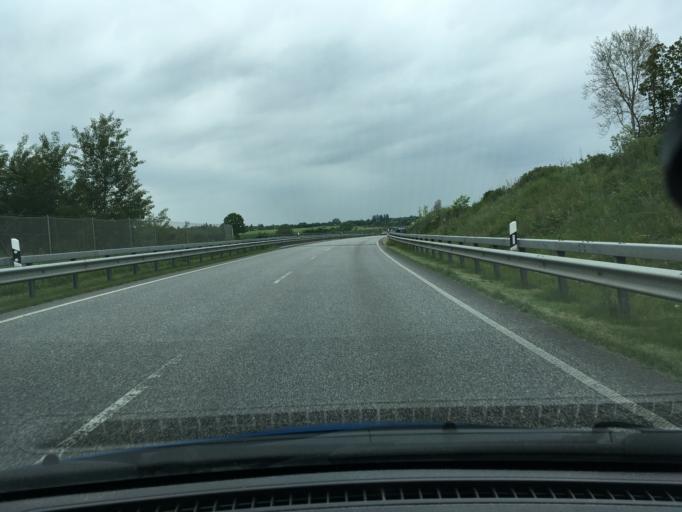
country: DE
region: Schleswig-Holstein
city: Pogeez
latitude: 53.7481
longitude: 10.7240
